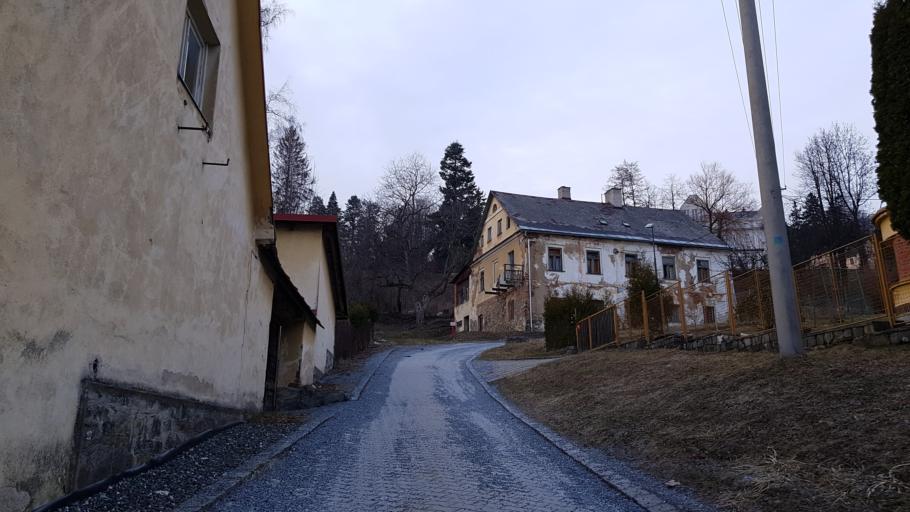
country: CZ
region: Olomoucky
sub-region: Okres Jesenik
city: Jesenik
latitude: 50.2372
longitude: 17.1864
